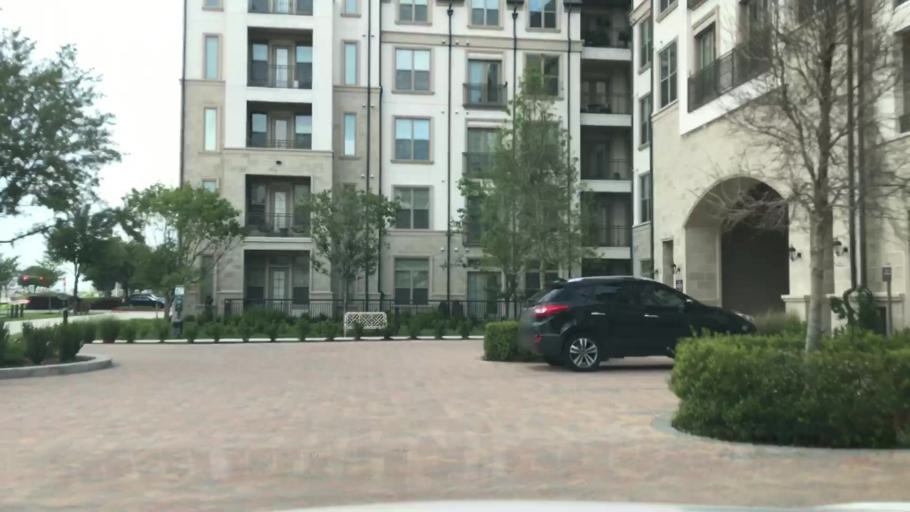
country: US
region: Texas
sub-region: Collin County
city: Frisco
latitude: 33.0889
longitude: -96.8031
